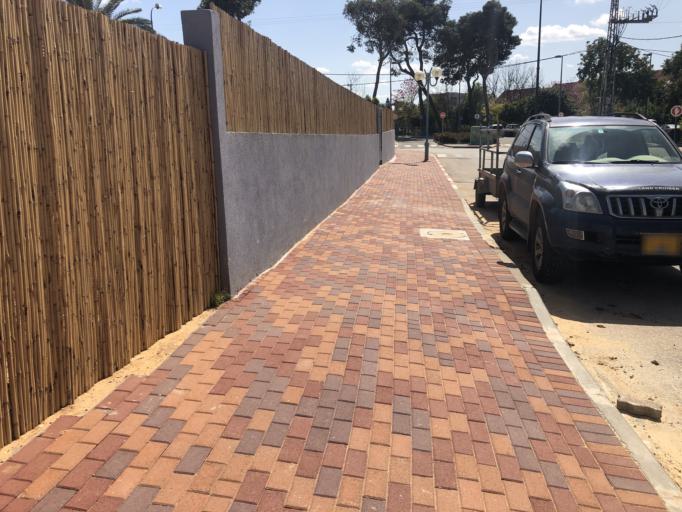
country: IL
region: Central District
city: Kfar Saba
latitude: 32.1577
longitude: 34.9201
